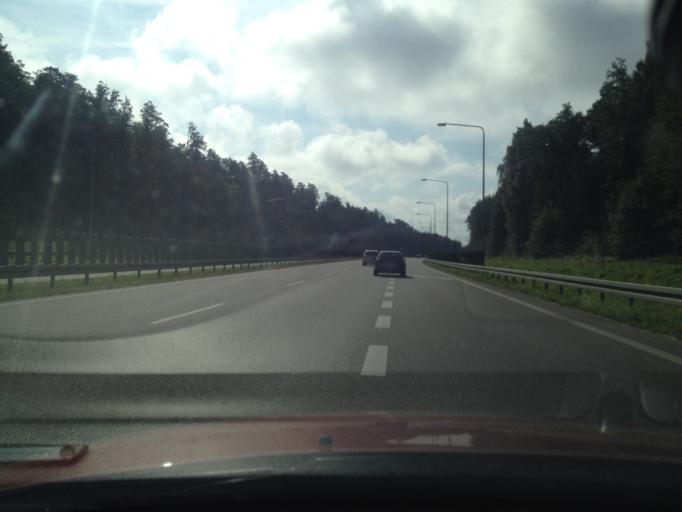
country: PL
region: West Pomeranian Voivodeship
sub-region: Powiat goleniowski
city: Przybiernow
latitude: 53.8320
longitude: 14.7492
